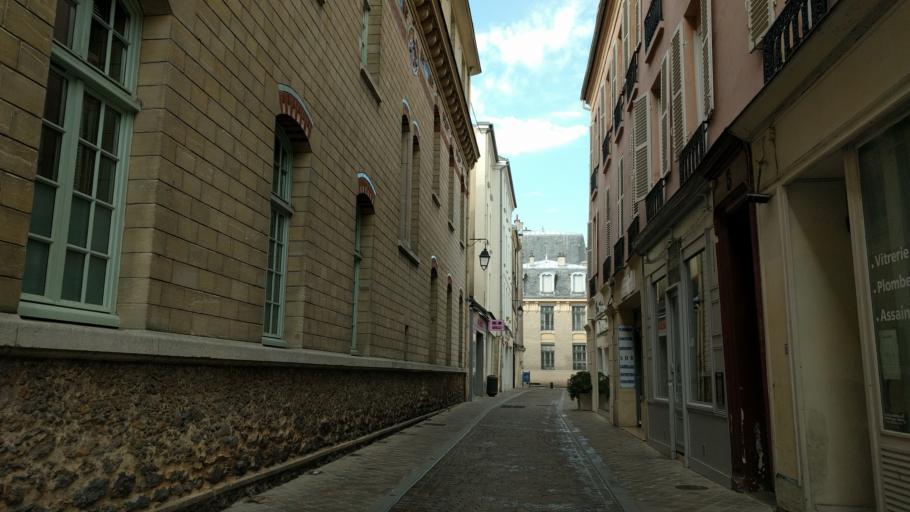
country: FR
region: Ile-de-France
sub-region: Departement des Yvelines
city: Saint-Germain-en-Laye
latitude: 48.8979
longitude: 2.0907
